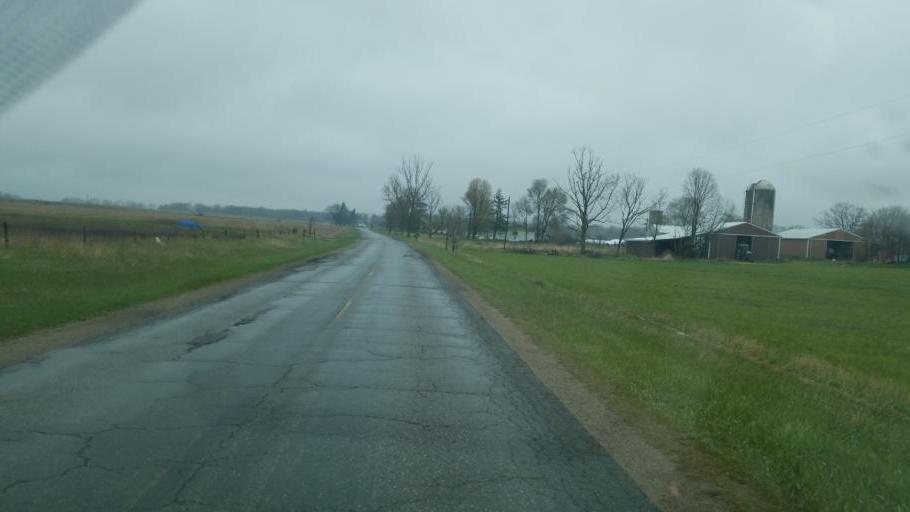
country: US
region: Michigan
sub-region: Mecosta County
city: Canadian Lakes
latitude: 43.5488
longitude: -85.3427
